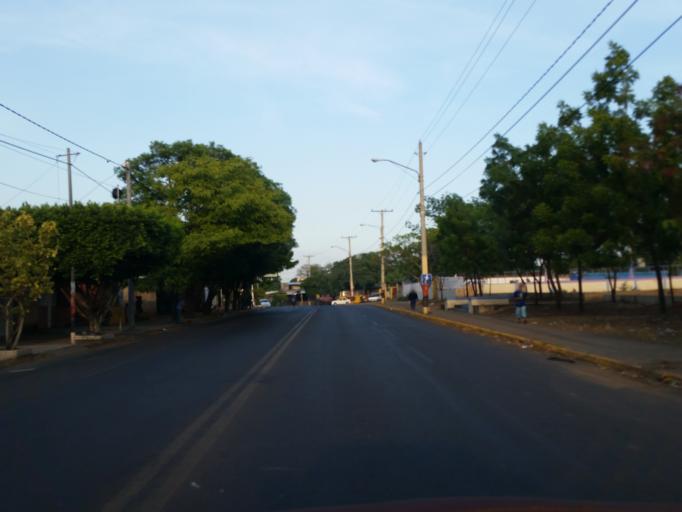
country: NI
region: Managua
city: Managua
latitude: 12.1377
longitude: -86.2615
